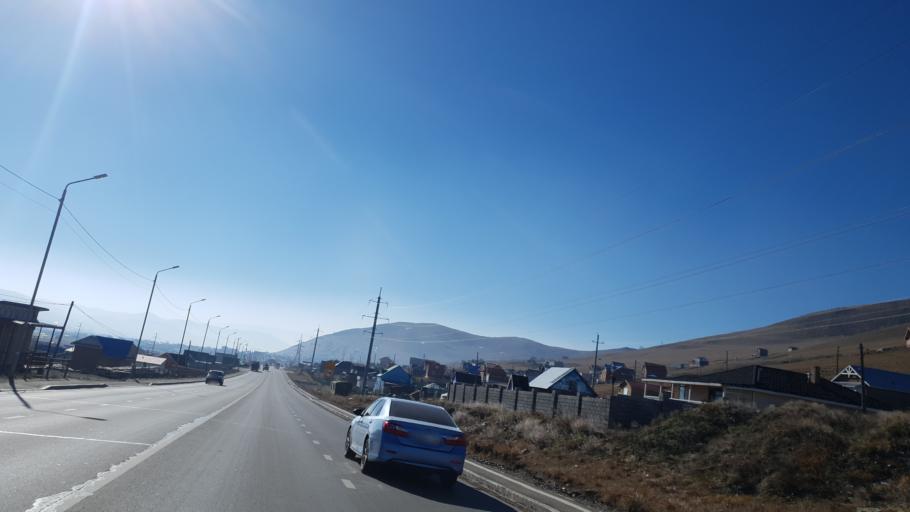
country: MN
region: Ulaanbaatar
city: Ulaanbaatar
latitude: 48.0281
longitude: 106.9119
